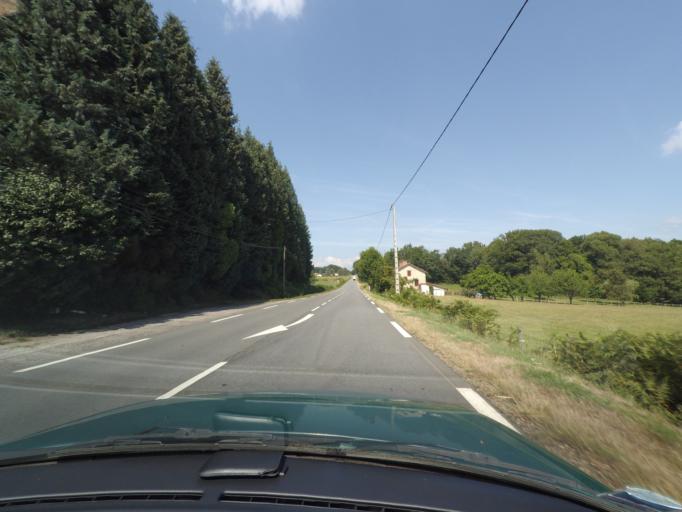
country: FR
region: Limousin
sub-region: Departement de la Haute-Vienne
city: Saint-Leonard-de-Noblat
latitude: 45.7842
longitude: 1.4770
